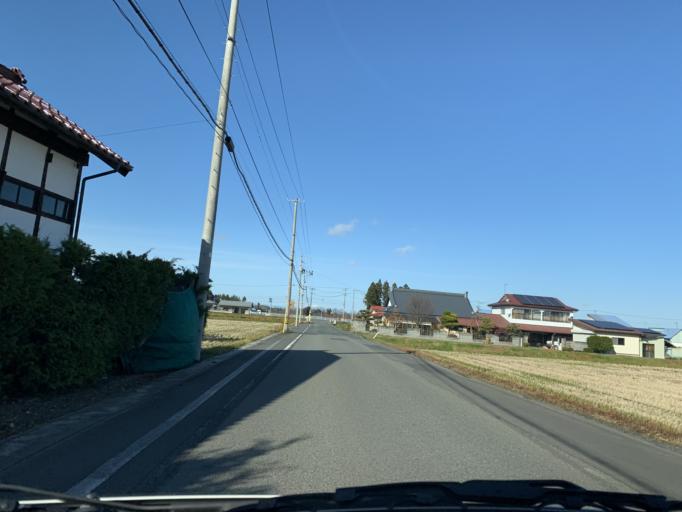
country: JP
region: Iwate
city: Mizusawa
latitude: 39.1620
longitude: 141.0991
